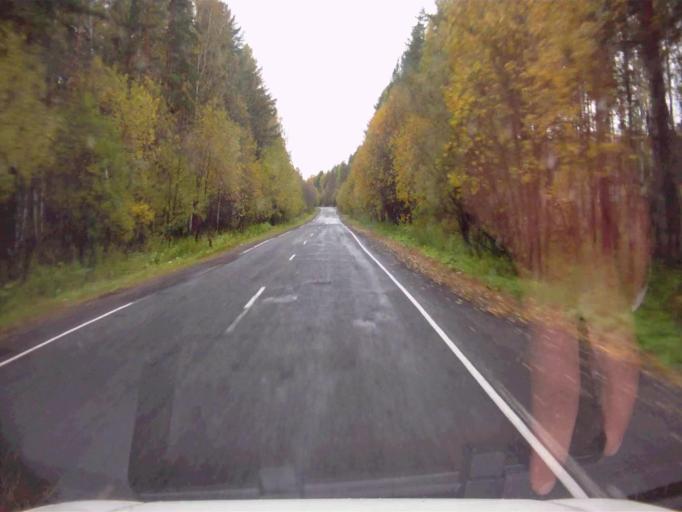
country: RU
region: Chelyabinsk
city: Verkhniy Ufaley
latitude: 56.0477
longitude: 60.1237
